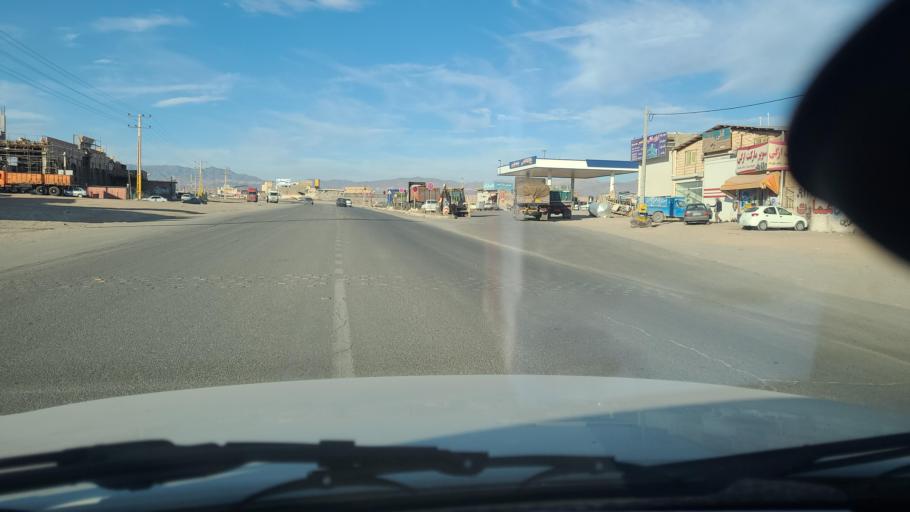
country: IR
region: Razavi Khorasan
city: Sabzevar
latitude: 36.2233
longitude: 57.6517
